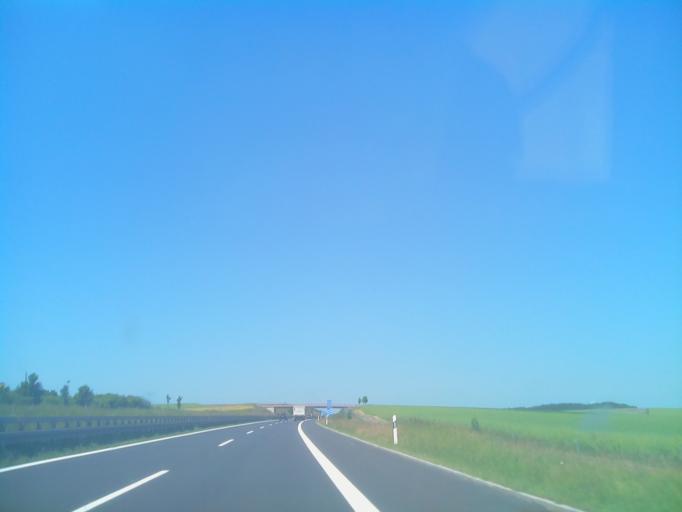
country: DE
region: Bavaria
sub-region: Regierungsbezirk Unterfranken
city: Oerlenbach
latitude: 50.1353
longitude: 10.1506
